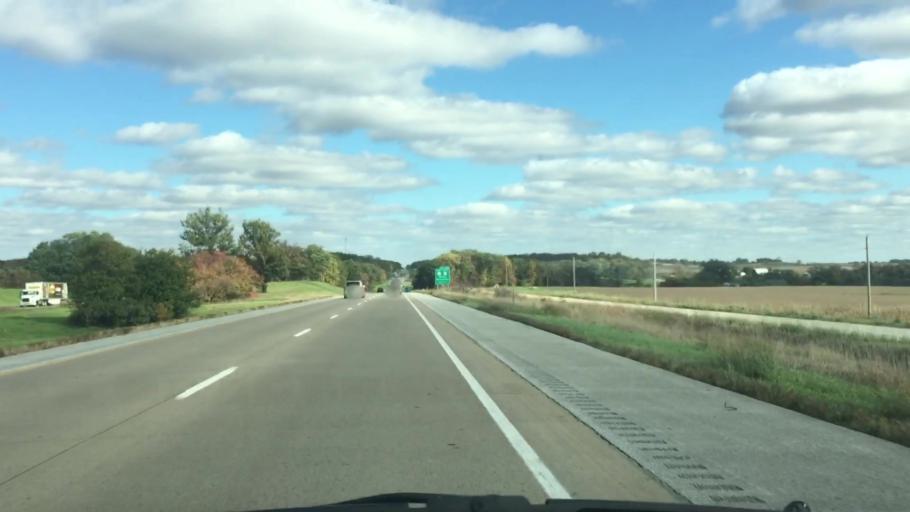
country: US
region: Iowa
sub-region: Muscatine County
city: Wilton
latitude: 41.6430
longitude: -91.0708
